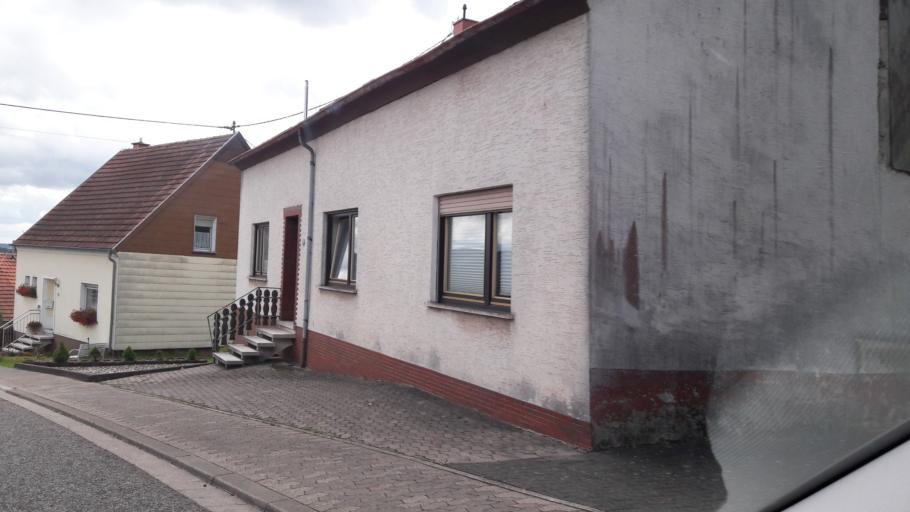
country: DE
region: Saarland
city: Tholey
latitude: 49.4990
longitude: 6.9682
